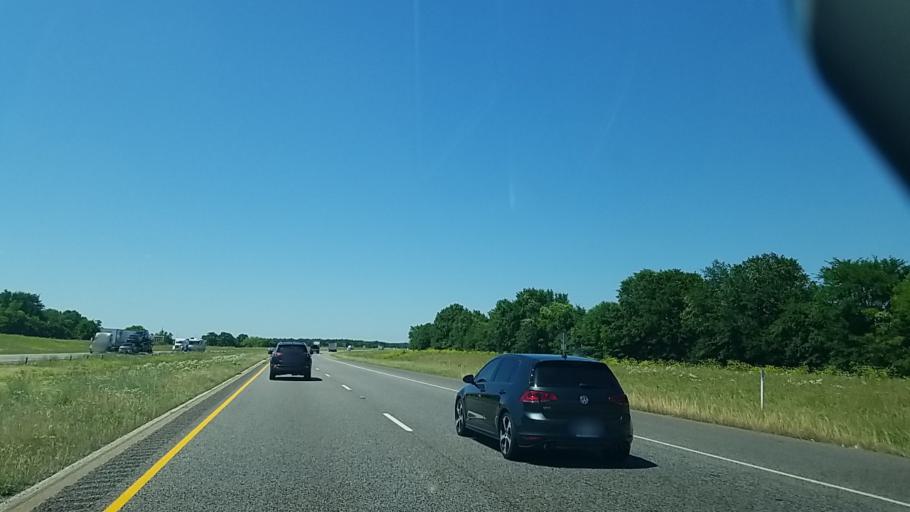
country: US
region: Texas
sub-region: Freestone County
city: Fairfield
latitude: 31.6011
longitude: -96.1552
